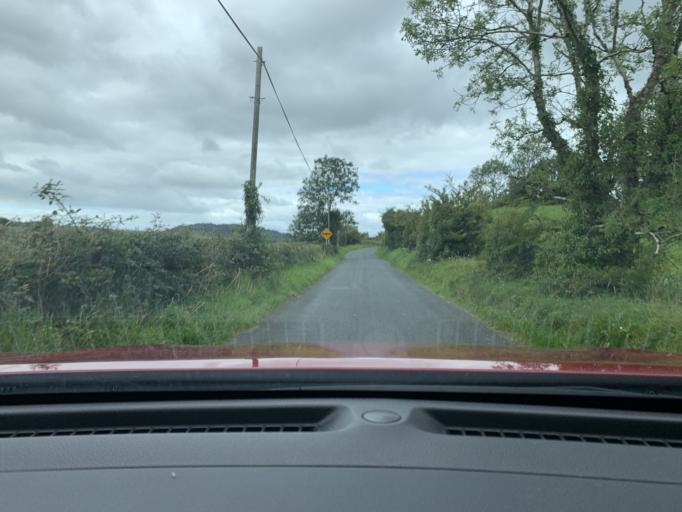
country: IE
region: Connaught
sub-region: Sligo
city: Collooney
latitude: 54.1878
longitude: -8.4520
